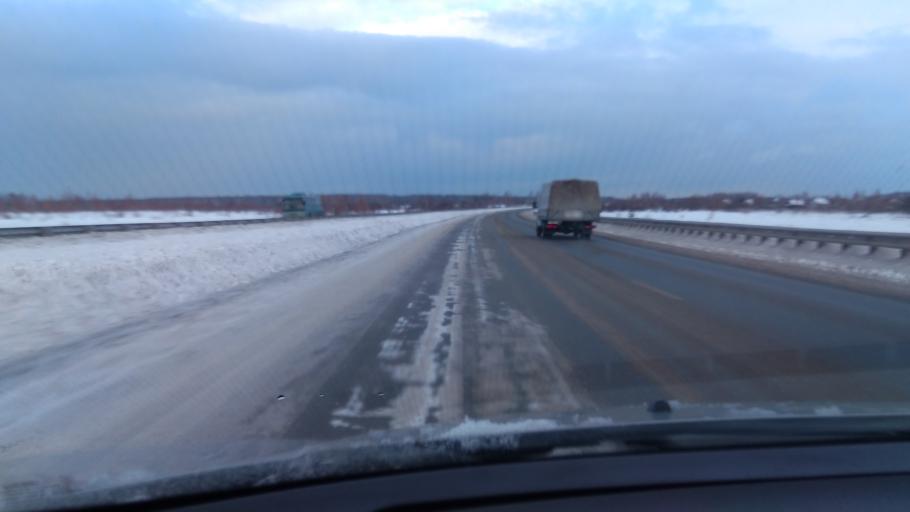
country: RU
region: Sverdlovsk
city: Nev'yansk
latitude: 57.5105
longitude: 60.1752
